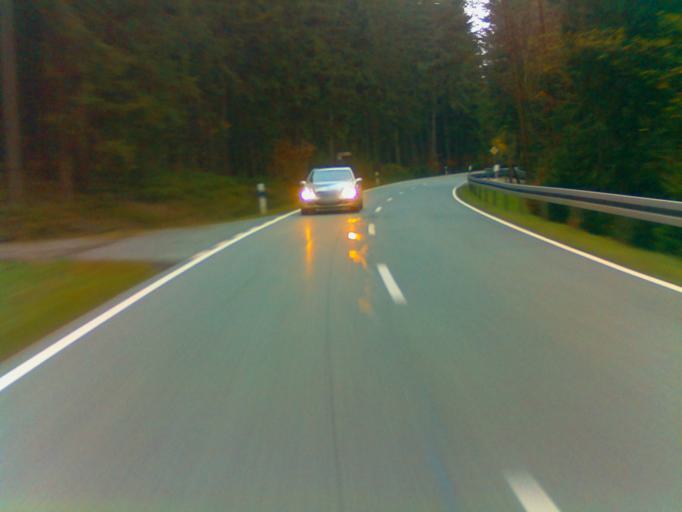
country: DE
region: Hesse
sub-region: Regierungsbezirk Darmstadt
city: Wald-Michelbach
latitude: 49.5966
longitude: 8.8773
